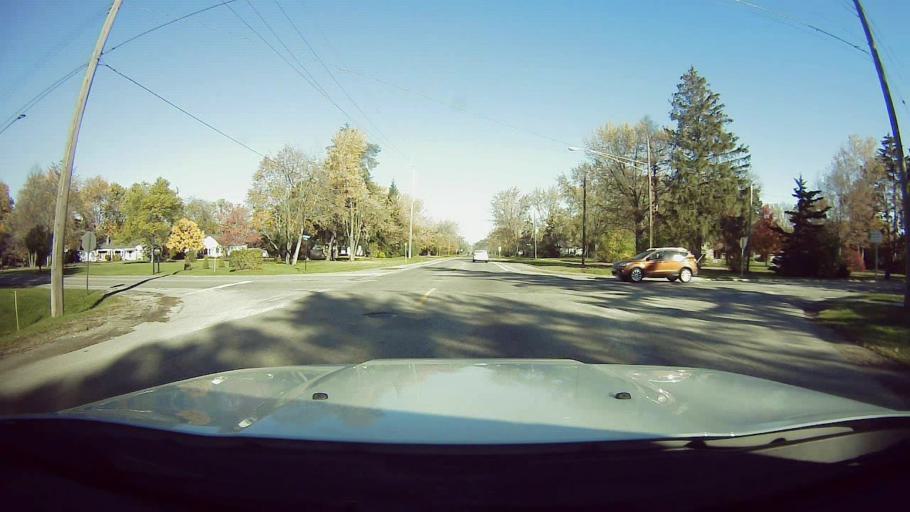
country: US
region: Michigan
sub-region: Oakland County
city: Beverly Hills
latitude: 42.5245
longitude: -83.2040
